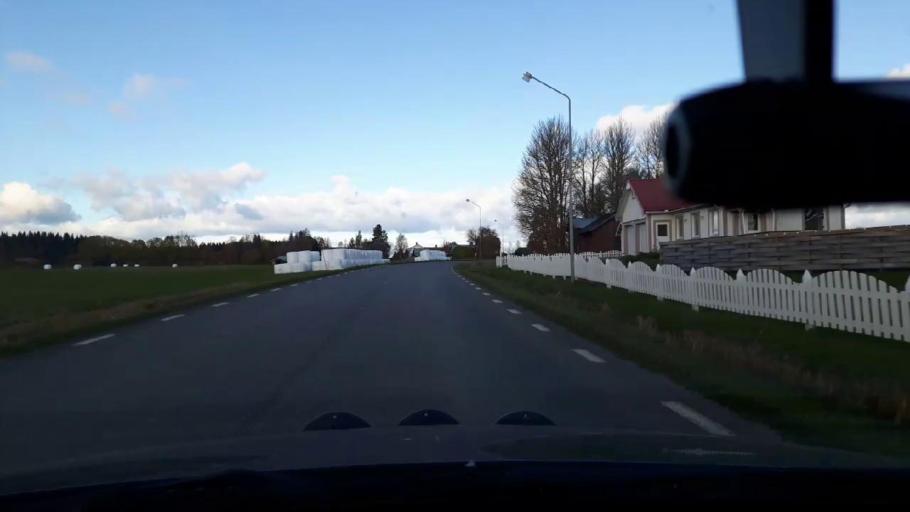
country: SE
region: Jaemtland
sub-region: Bergs Kommun
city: Hoverberg
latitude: 63.0106
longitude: 14.3404
